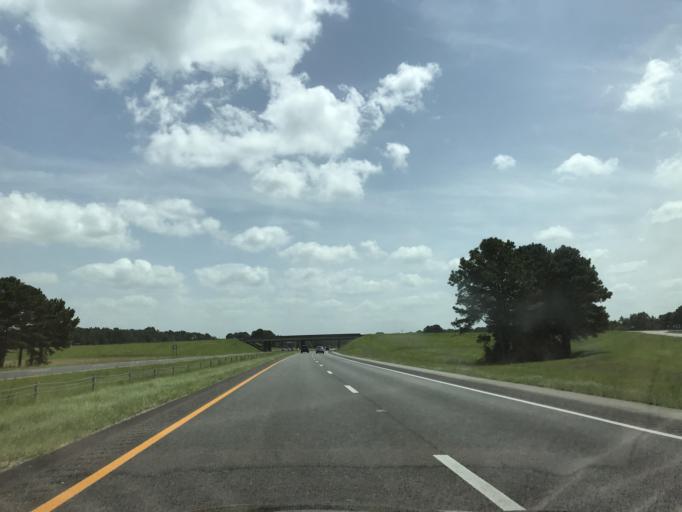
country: US
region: North Carolina
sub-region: Wayne County
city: Mount Olive
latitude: 35.1189
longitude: -78.1886
